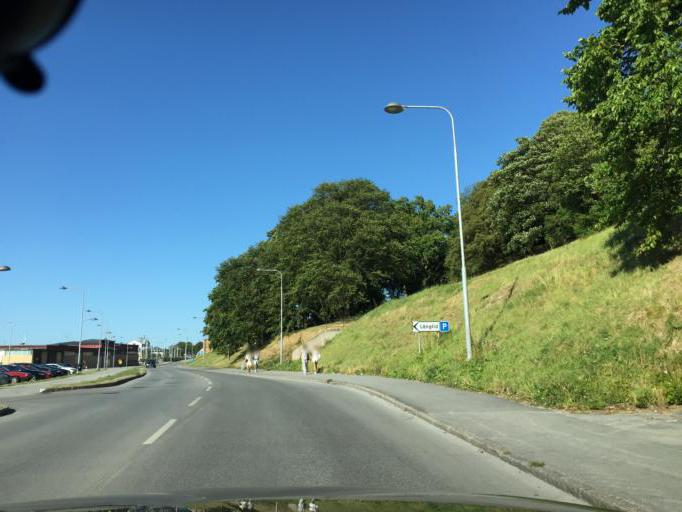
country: SE
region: Gotland
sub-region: Gotland
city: Visby
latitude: 57.6347
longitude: 18.2833
